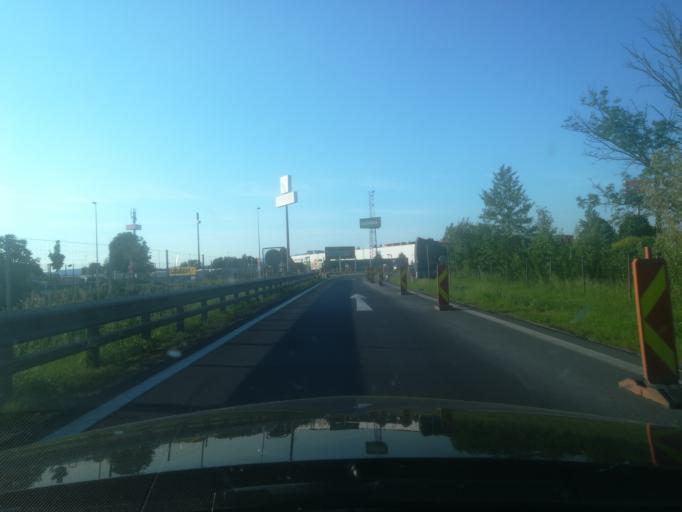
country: AT
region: Upper Austria
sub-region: Politischer Bezirk Linz-Land
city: Ansfelden
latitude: 48.2134
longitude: 14.2850
